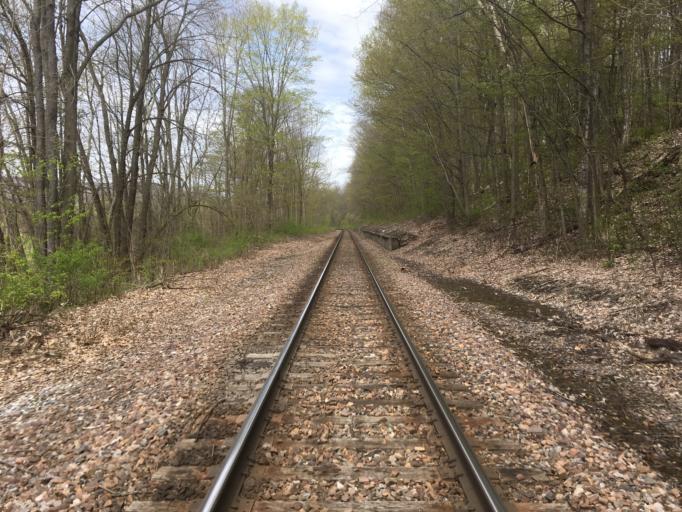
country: US
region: Vermont
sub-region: Rutland County
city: Brandon
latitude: 43.7119
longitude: -73.0393
